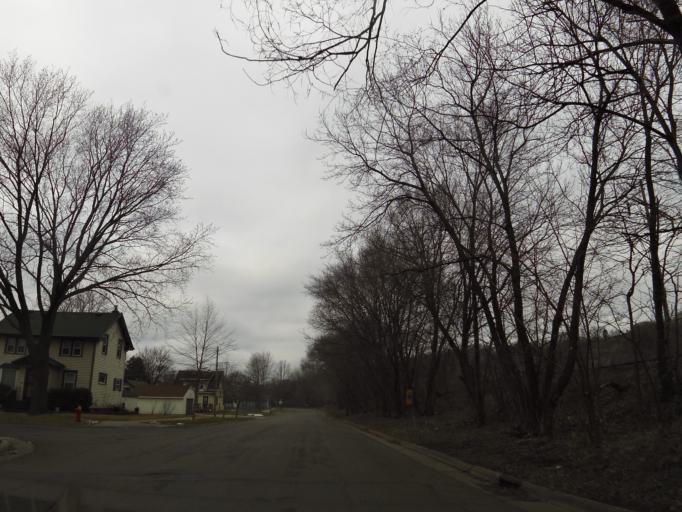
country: US
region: Minnesota
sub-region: Dakota County
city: West Saint Paul
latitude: 44.9324
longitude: -93.1267
